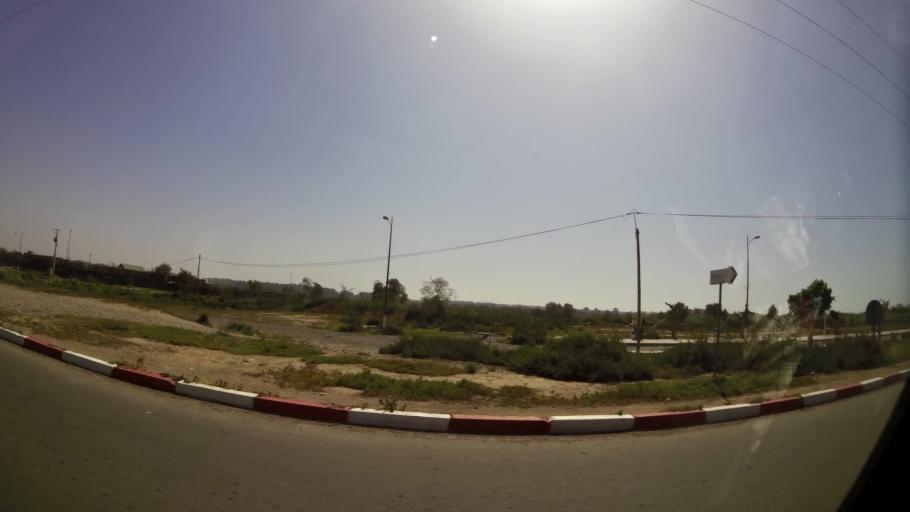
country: MA
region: Souss-Massa-Draa
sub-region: Inezgane-Ait Mellou
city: Inezgane
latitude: 30.3569
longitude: -9.5644
